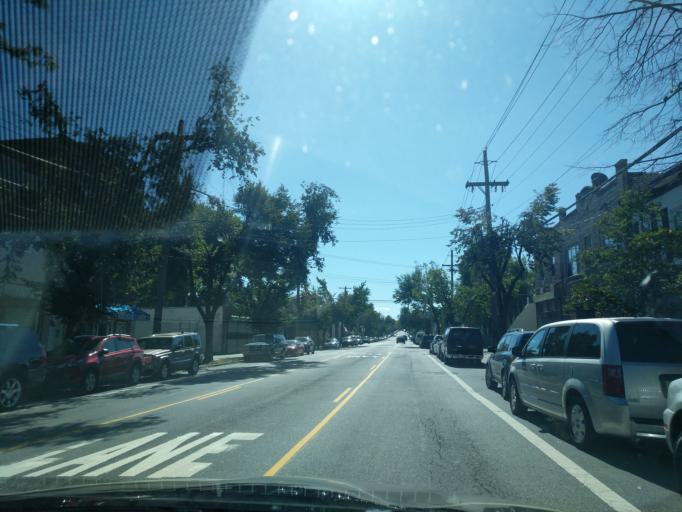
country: US
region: New York
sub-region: Westchester County
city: Pelham Manor
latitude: 40.8464
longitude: -73.7863
